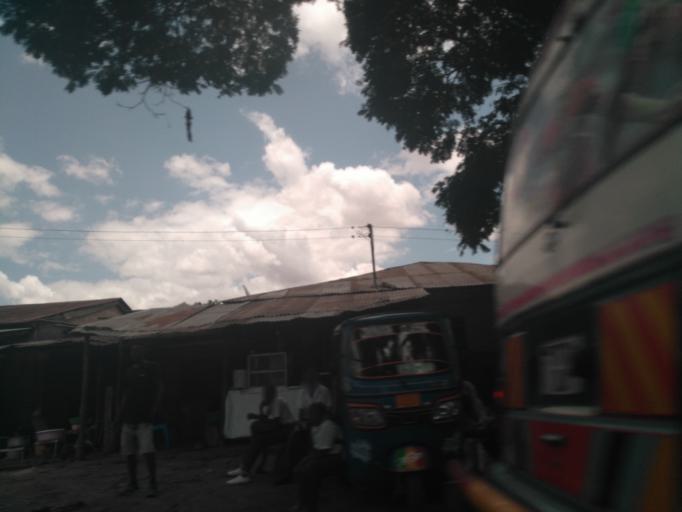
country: TZ
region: Dar es Salaam
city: Dar es Salaam
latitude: -6.8662
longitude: 39.2701
